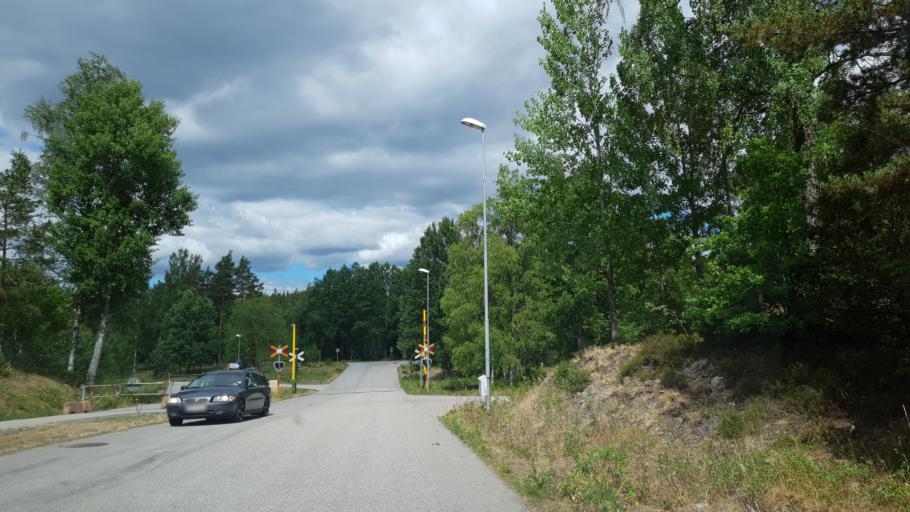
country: SE
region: Kronoberg
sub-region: Uppvidinge Kommun
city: Aseda
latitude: 57.1709
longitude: 15.3693
